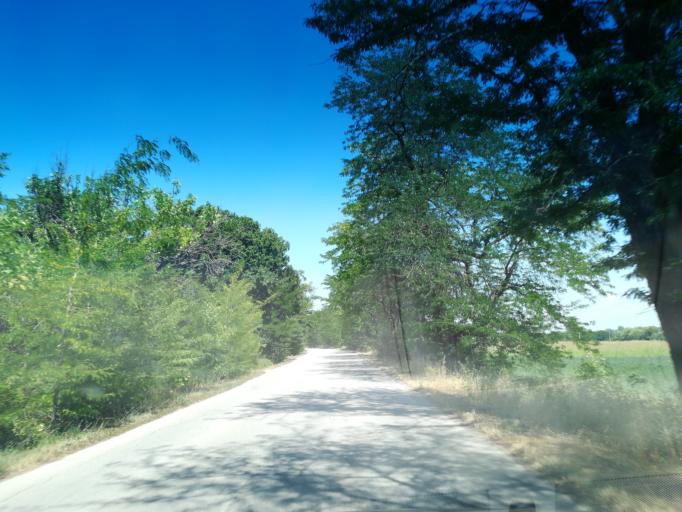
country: BG
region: Plovdiv
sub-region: Obshtina Sadovo
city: Sadovo
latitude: 42.0204
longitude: 25.0880
